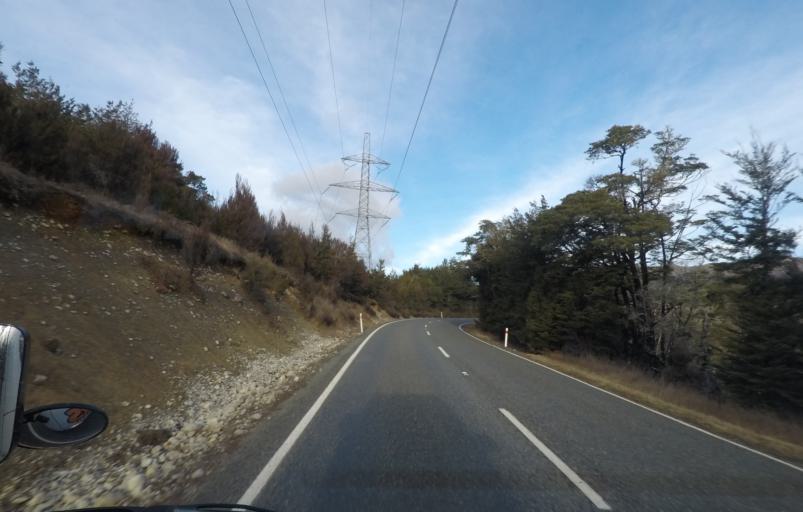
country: NZ
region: Tasman
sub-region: Tasman District
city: Wakefield
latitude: -41.7650
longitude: 172.8937
